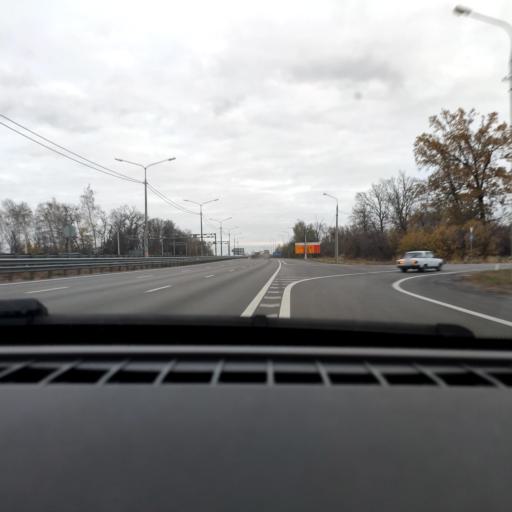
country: RU
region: Voronezj
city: Podgornoye
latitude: 51.8301
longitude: 39.2129
